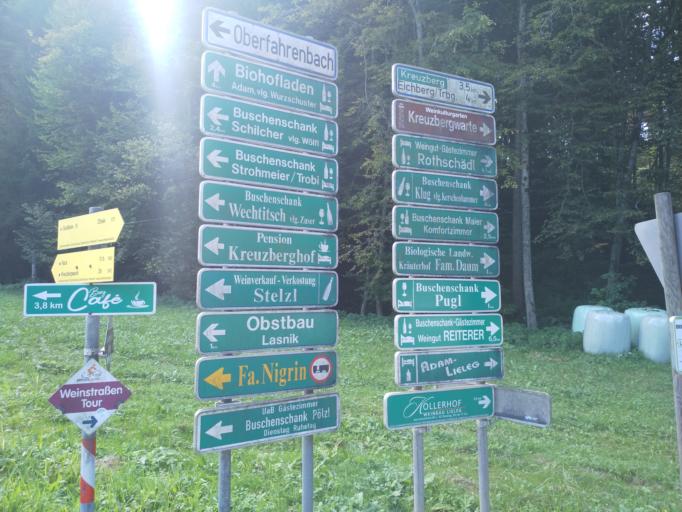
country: AT
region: Styria
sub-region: Politischer Bezirk Leibnitz
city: Grossklein
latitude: 46.7288
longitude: 15.4590
